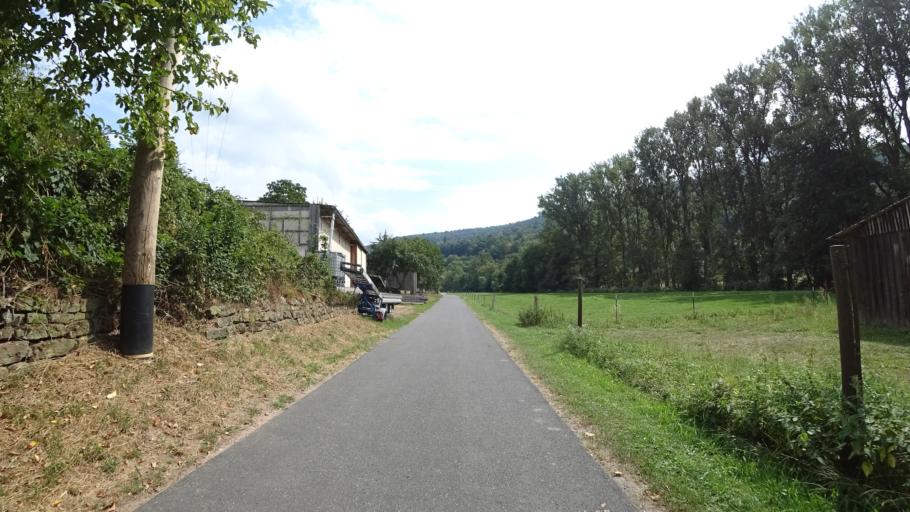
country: DE
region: Bavaria
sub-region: Regierungsbezirk Unterfranken
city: Miltenberg
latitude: 49.7063
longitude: 9.2839
